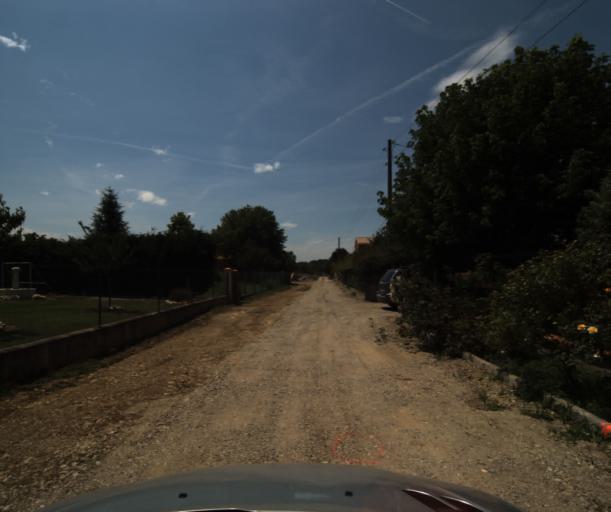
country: FR
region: Midi-Pyrenees
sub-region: Departement de la Haute-Garonne
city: Labastidette
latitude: 43.4513
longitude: 1.2416
